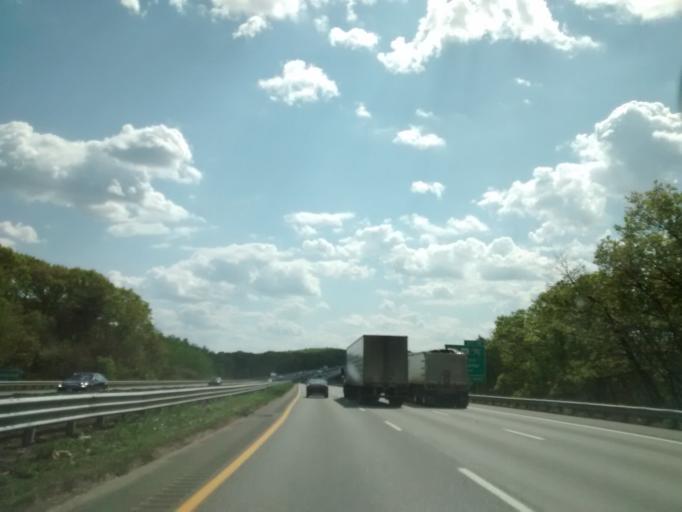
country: US
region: Massachusetts
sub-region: Worcester County
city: Auburn
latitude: 42.1994
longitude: -71.8389
